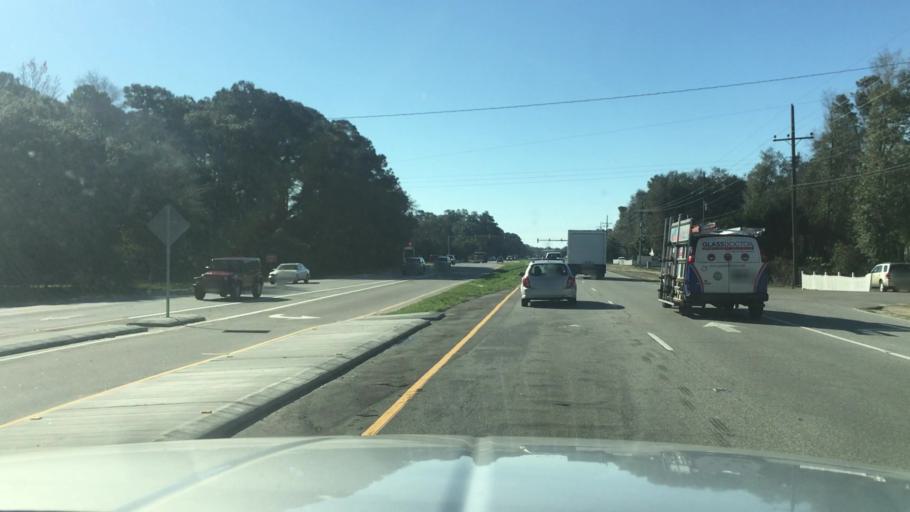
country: US
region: North Carolina
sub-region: New Hanover County
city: Sea Breeze
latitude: 34.0913
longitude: -77.8970
